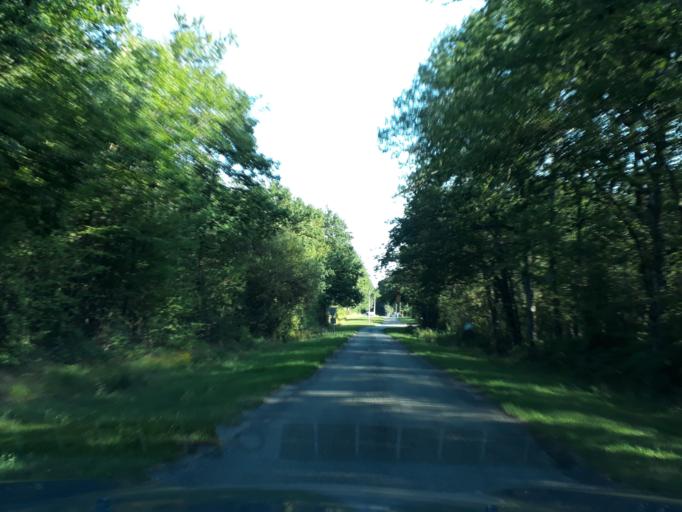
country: FR
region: Centre
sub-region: Departement du Loiret
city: Huisseau-sur-Mauves
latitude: 47.9294
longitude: 1.7426
